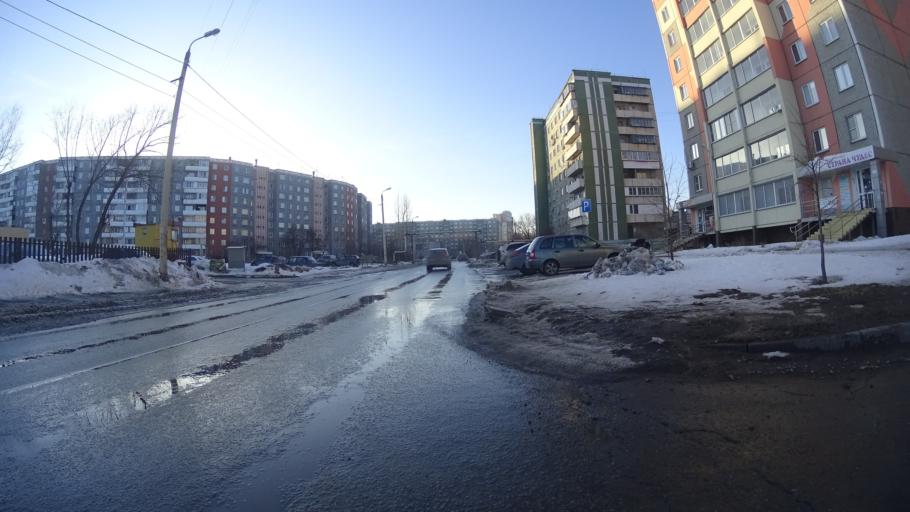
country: RU
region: Chelyabinsk
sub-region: Gorod Chelyabinsk
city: Chelyabinsk
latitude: 55.1362
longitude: 61.4519
